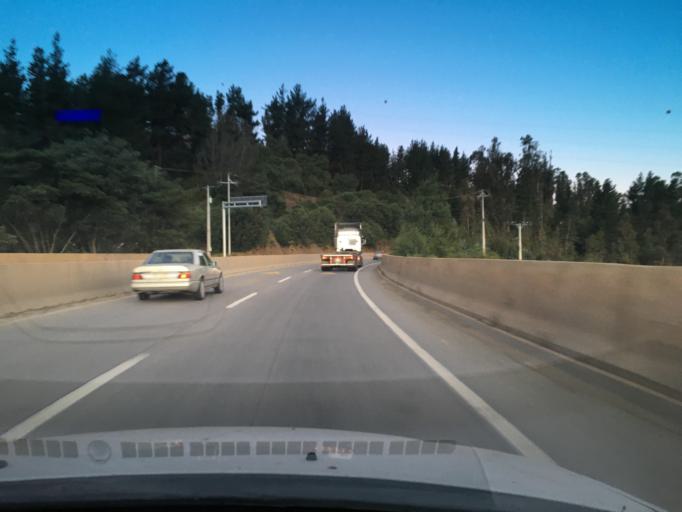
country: CL
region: Valparaiso
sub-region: Provincia de Valparaiso
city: Vina del Mar
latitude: -33.1059
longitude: -71.5608
